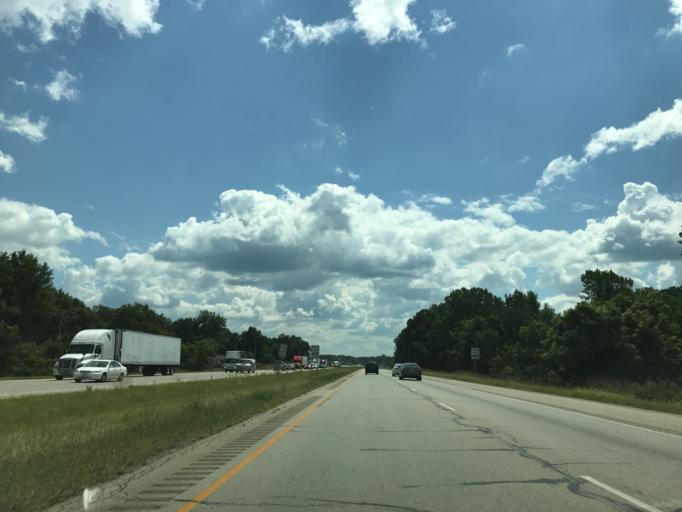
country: US
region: Indiana
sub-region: Kosciusko County
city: Winona Lake
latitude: 41.2463
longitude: -85.8228
